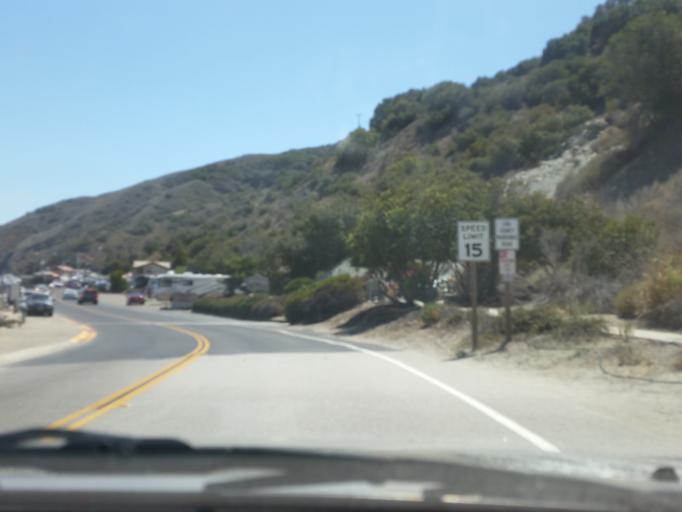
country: US
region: California
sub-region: San Luis Obispo County
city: Avila Beach
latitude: 35.1745
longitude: -120.7558
